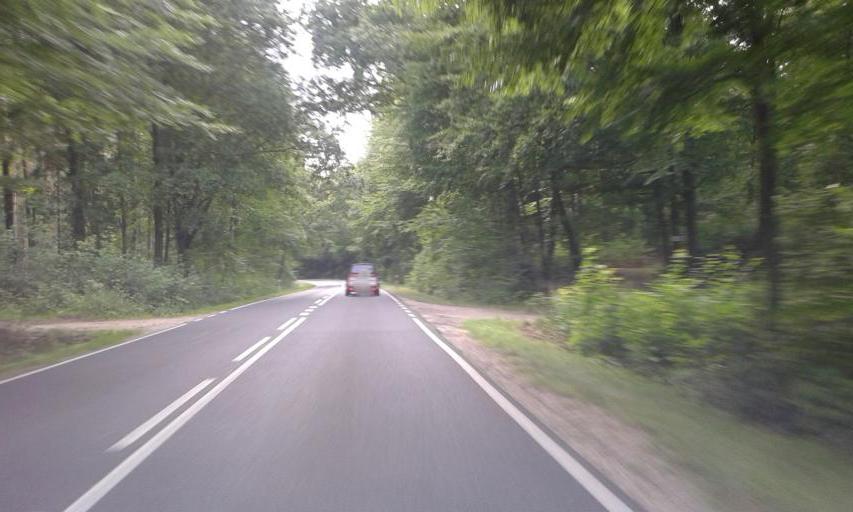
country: PL
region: West Pomeranian Voivodeship
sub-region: Powiat szczecinecki
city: Grzmiaca
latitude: 53.7221
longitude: 16.5169
